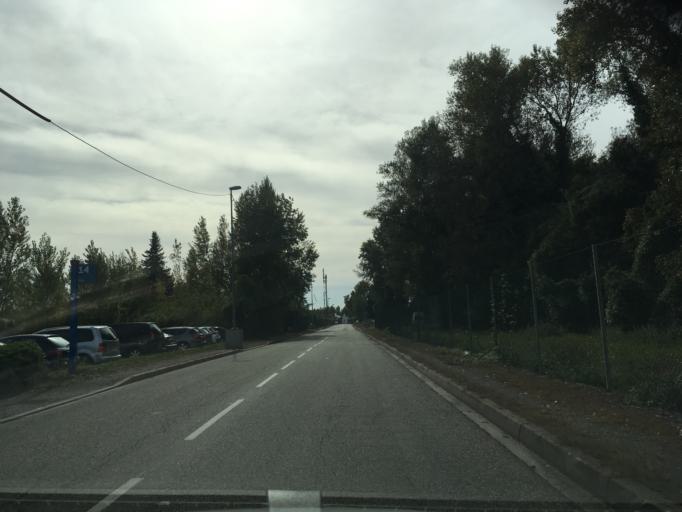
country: DE
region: Baden-Wuerttemberg
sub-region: Freiburg Region
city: Kehl
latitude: 48.5971
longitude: 7.7987
